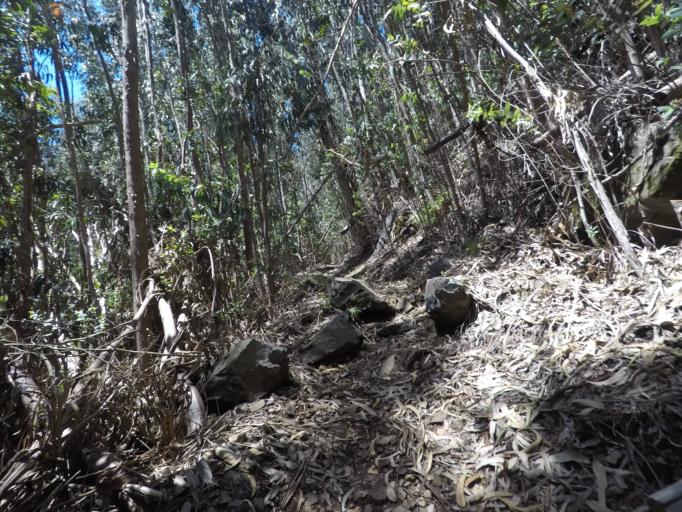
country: PT
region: Madeira
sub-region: Camara de Lobos
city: Curral das Freiras
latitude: 32.7500
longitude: -16.9702
